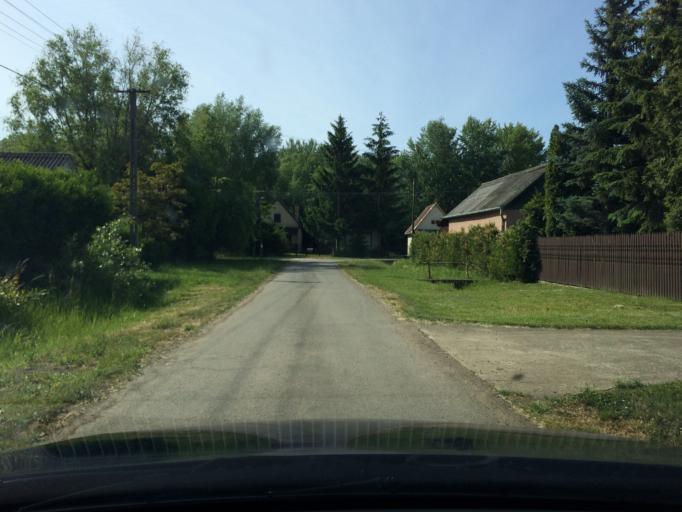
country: HU
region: Szabolcs-Szatmar-Bereg
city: Tiszavasvari
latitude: 47.9528
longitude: 21.3493
